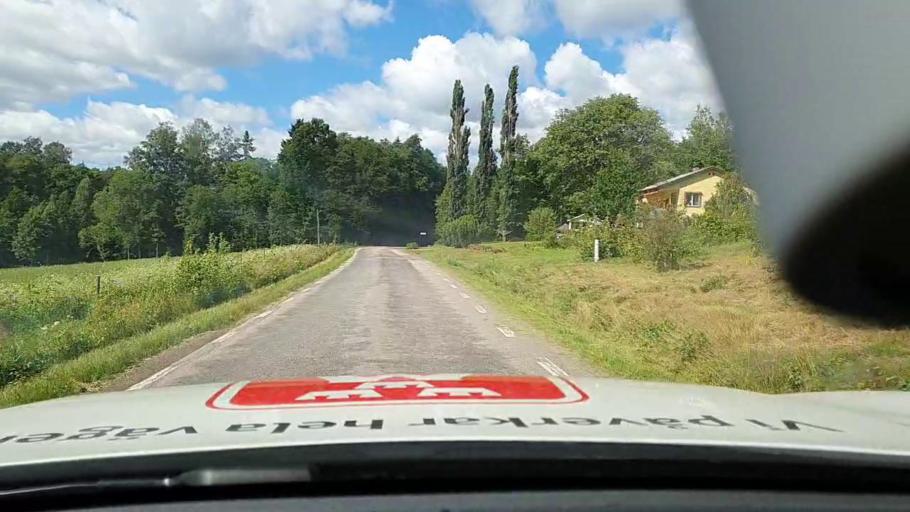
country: SE
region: Vaestra Goetaland
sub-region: Karlsborgs Kommun
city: Molltorp
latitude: 58.5904
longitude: 14.2660
